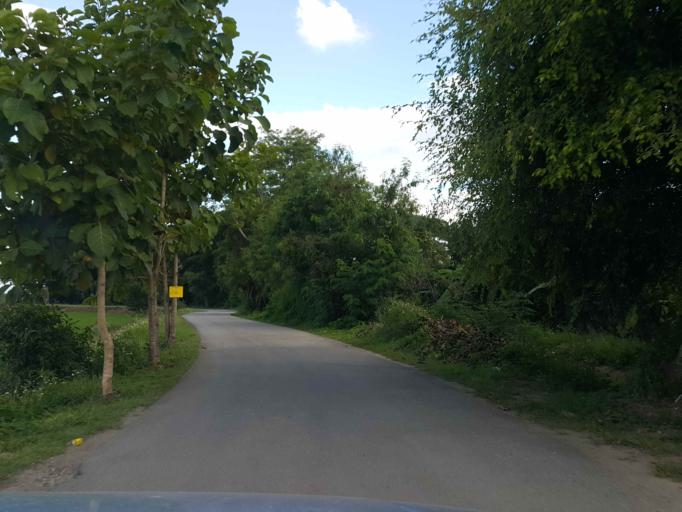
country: TH
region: Chiang Mai
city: San Sai
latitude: 18.9118
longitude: 98.9778
